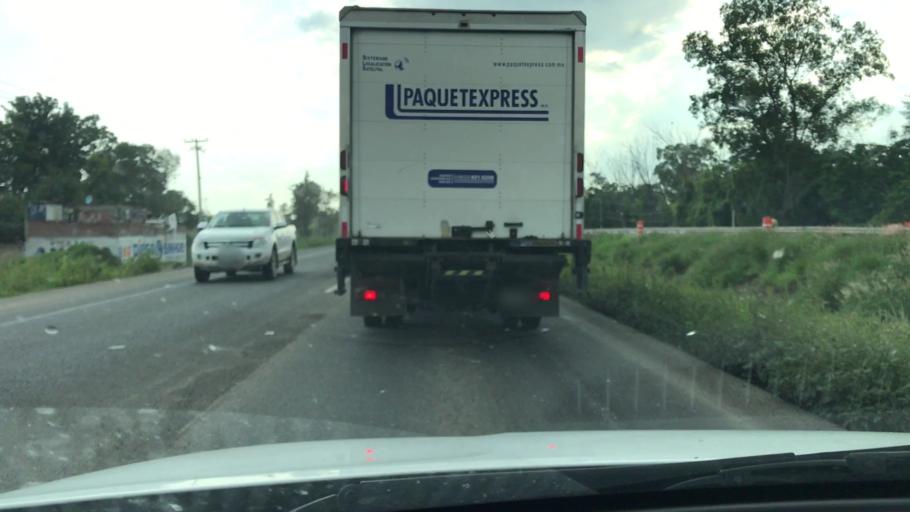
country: MX
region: Guanajuato
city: Irapuato
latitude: 20.6513
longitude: -101.3280
